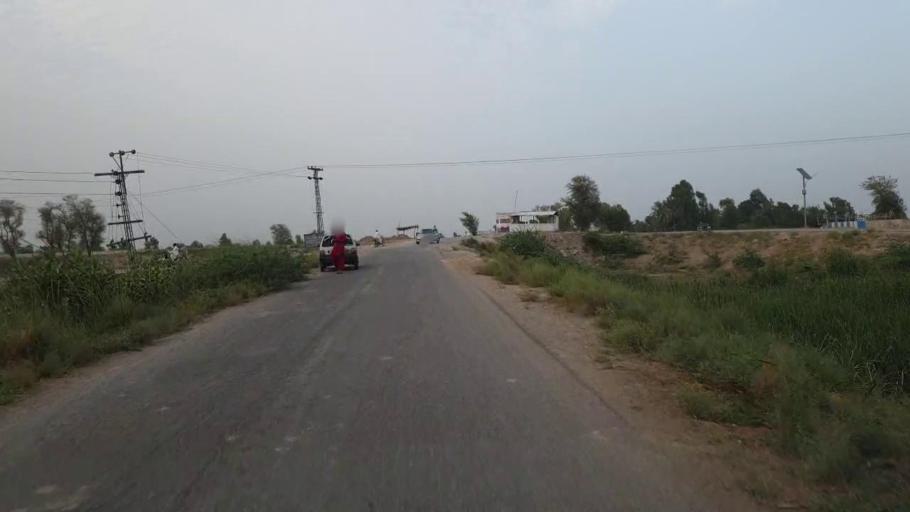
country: PK
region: Sindh
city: Daur
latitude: 26.4564
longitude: 68.2948
